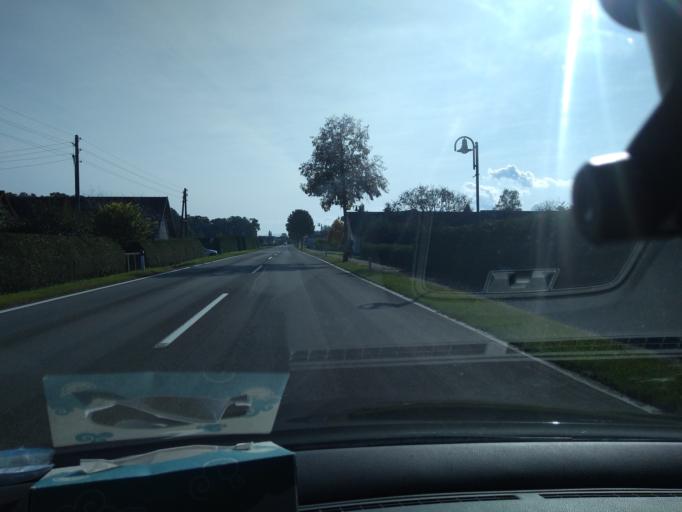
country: AT
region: Styria
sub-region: Politischer Bezirk Leibnitz
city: Lang
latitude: 46.8331
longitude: 15.5429
